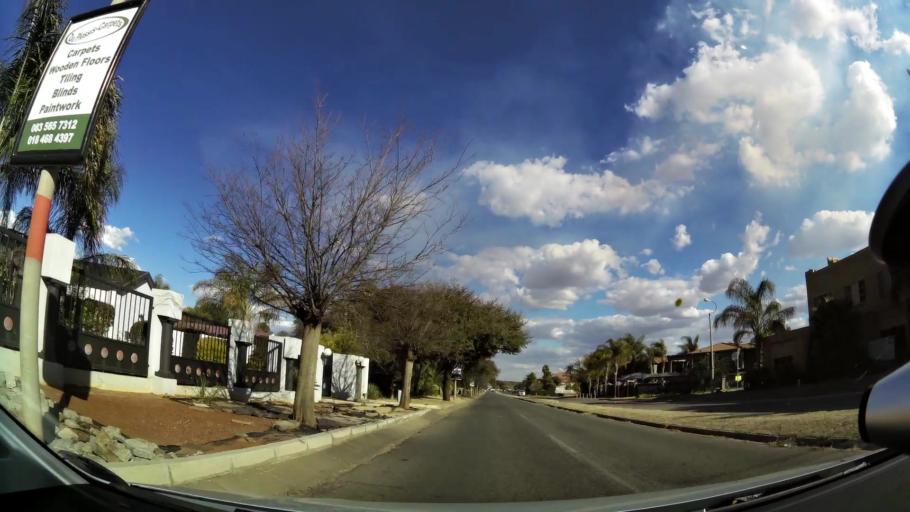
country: ZA
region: North-West
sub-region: Dr Kenneth Kaunda District Municipality
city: Klerksdorp
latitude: -26.8325
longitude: 26.6790
